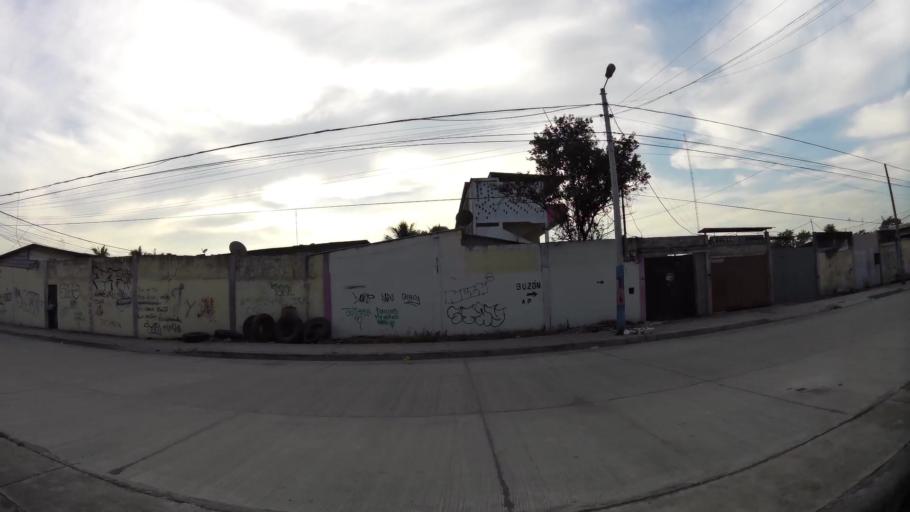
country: EC
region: Guayas
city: Eloy Alfaro
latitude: -2.0944
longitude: -79.9030
